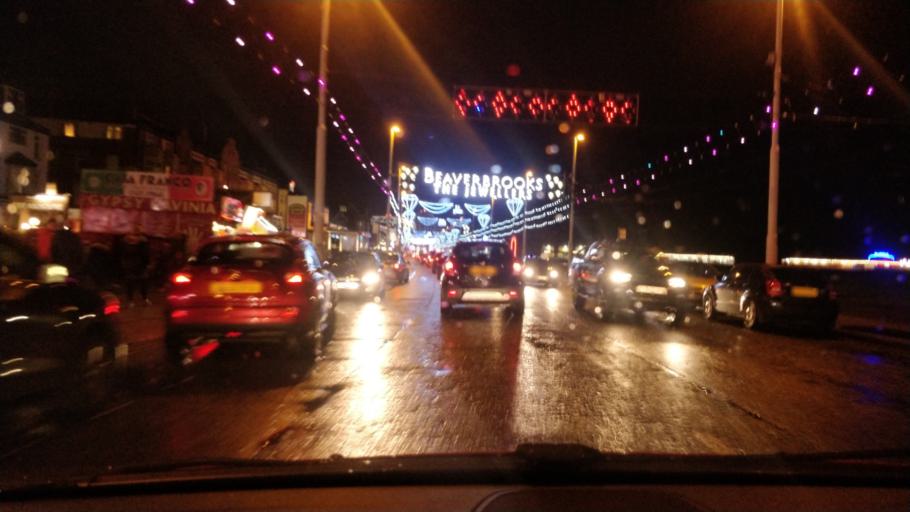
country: GB
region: England
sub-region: Blackpool
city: Blackpool
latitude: 53.7982
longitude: -3.0558
